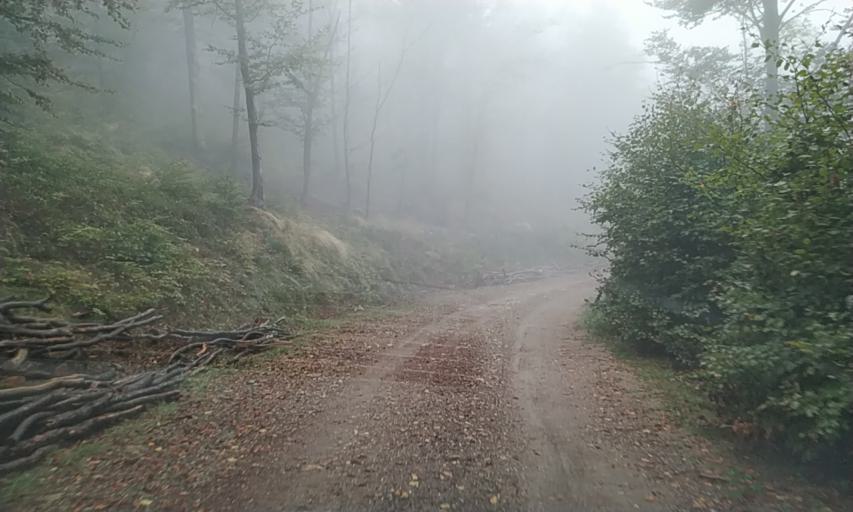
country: IT
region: Piedmont
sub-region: Provincia Verbano-Cusio-Ossola
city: Quarna Sotto
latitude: 45.8492
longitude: 8.3283
